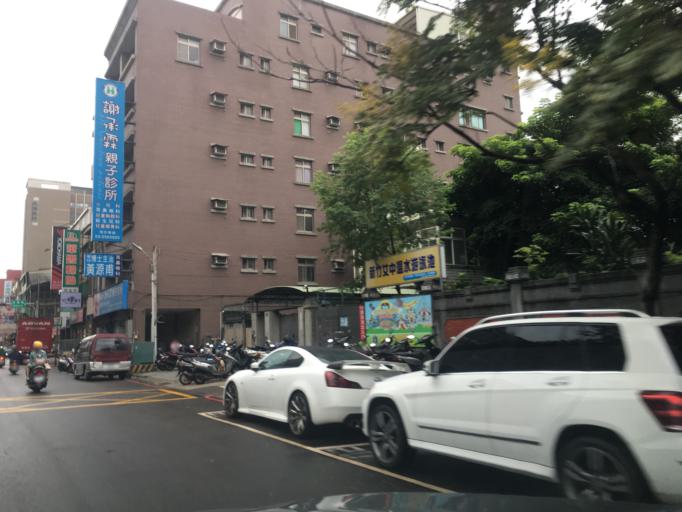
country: TW
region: Taiwan
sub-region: Hsinchu
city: Hsinchu
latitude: 24.8066
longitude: 120.9752
